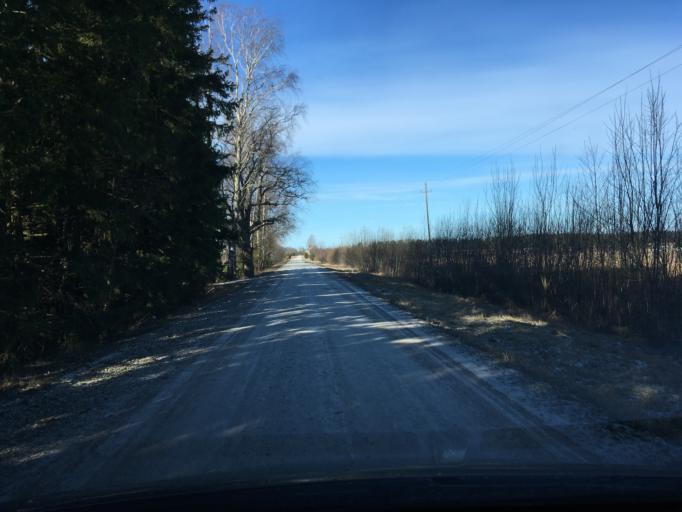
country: EE
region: Laeaene
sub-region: Lihula vald
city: Lihula
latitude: 58.5675
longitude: 23.6836
